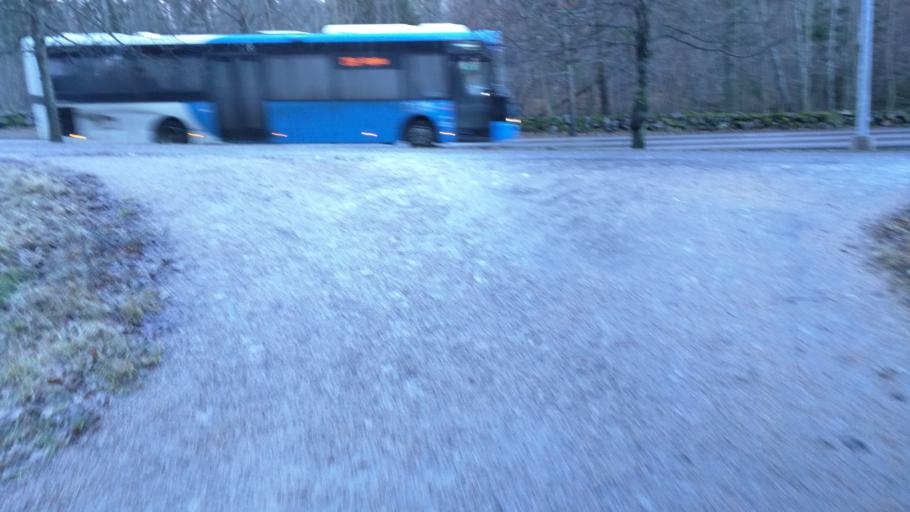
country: FI
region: Uusimaa
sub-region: Helsinki
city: Kauniainen
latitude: 60.2361
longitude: 24.7142
